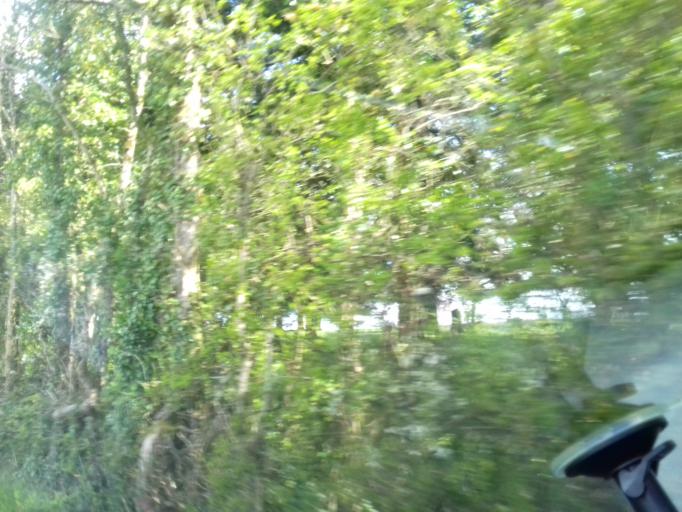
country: GB
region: Northern Ireland
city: Lisnaskea
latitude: 54.1864
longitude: -7.4887
